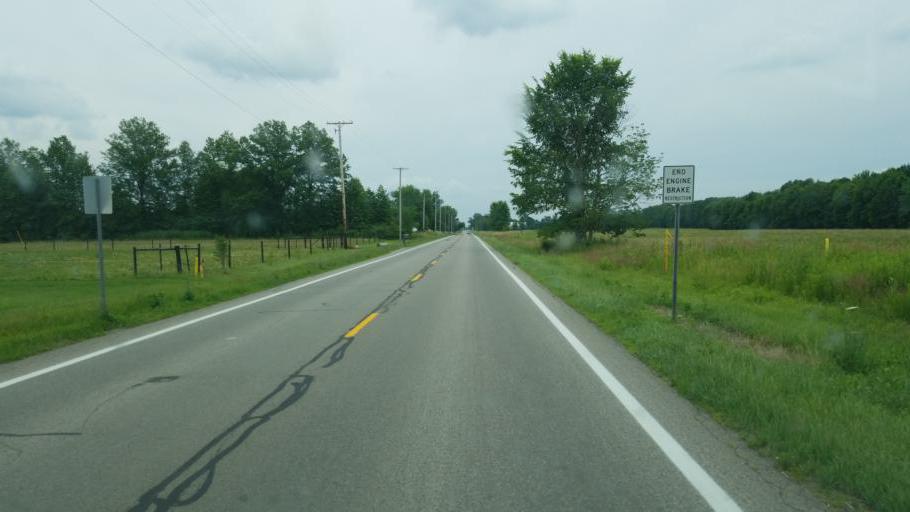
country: US
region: Ohio
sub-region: Ashtabula County
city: Orwell
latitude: 41.4616
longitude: -80.8589
